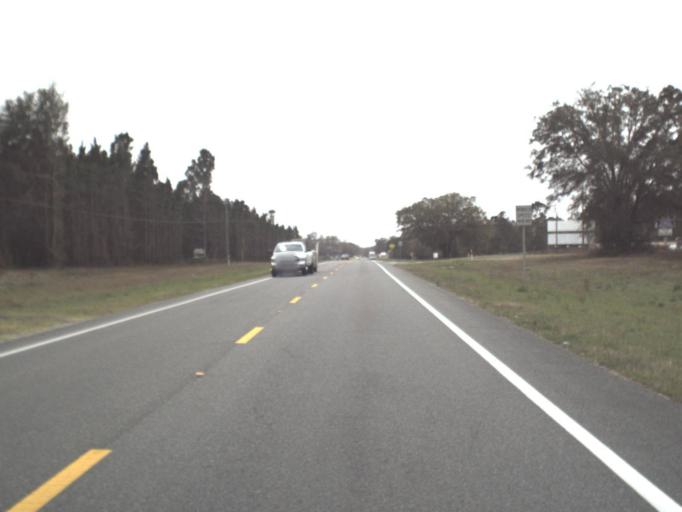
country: US
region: Florida
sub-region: Wakulla County
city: Crawfordville
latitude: 30.1122
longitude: -84.3754
